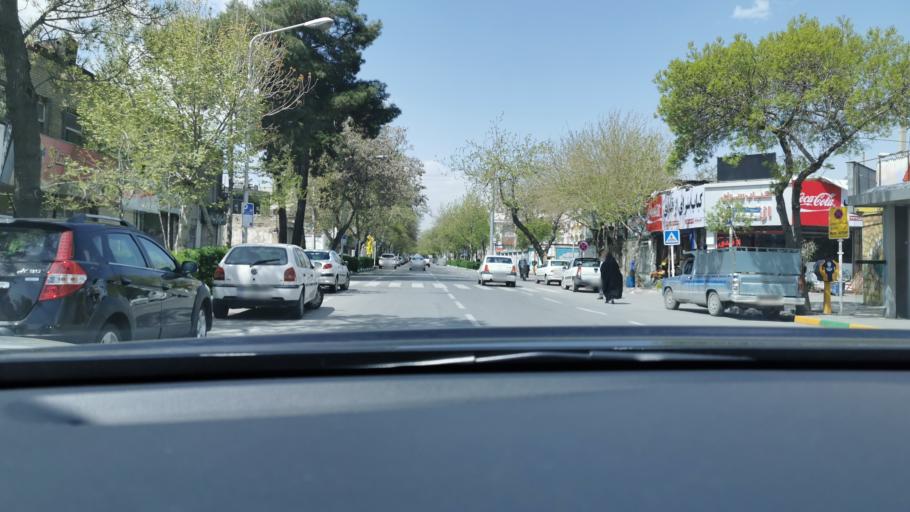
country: IR
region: Razavi Khorasan
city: Mashhad
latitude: 36.2961
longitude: 59.5981
